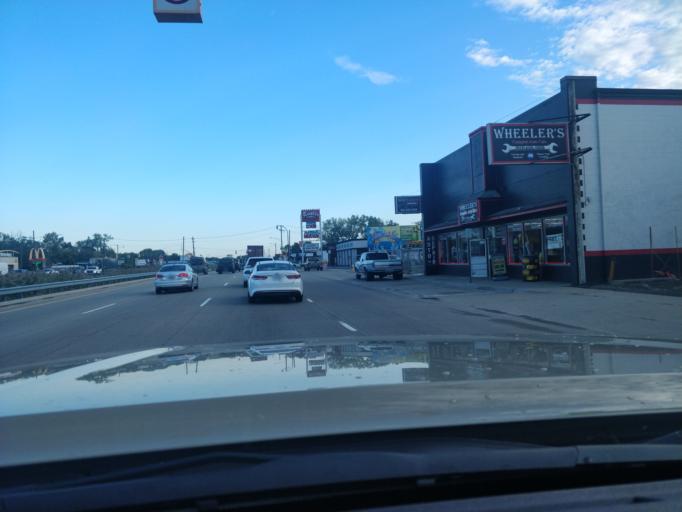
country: US
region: Michigan
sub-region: Wayne County
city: Southgate
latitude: 42.2213
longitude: -83.1809
